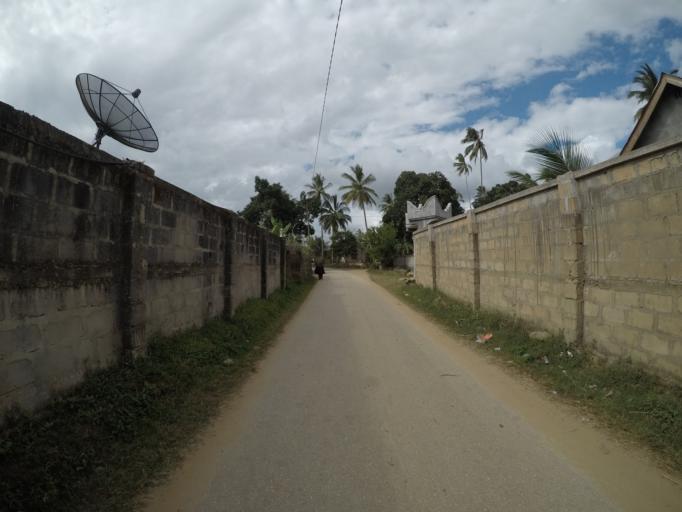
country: TZ
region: Zanzibar Central/South
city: Koani
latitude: -6.1938
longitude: 39.2644
